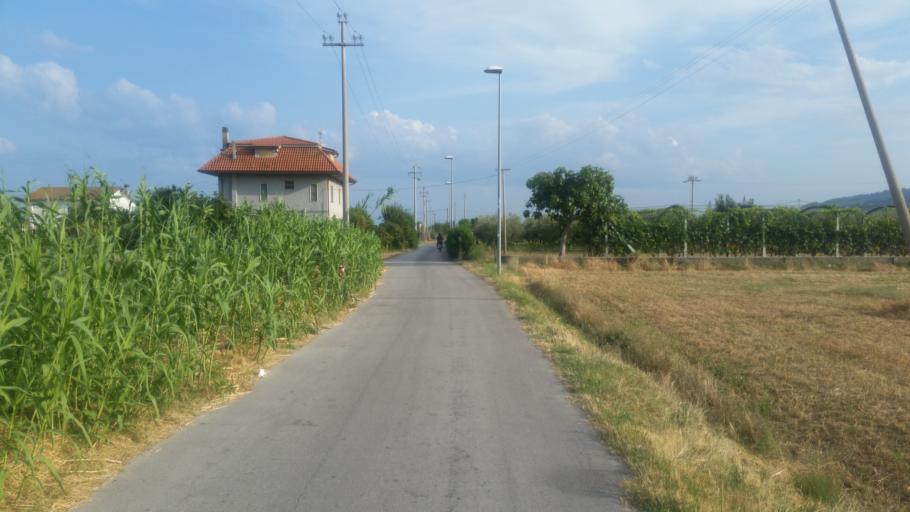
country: IT
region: The Marches
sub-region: Provincia di Ascoli Piceno
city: San Benedetto del Tronto
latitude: 42.9062
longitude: 13.9026
